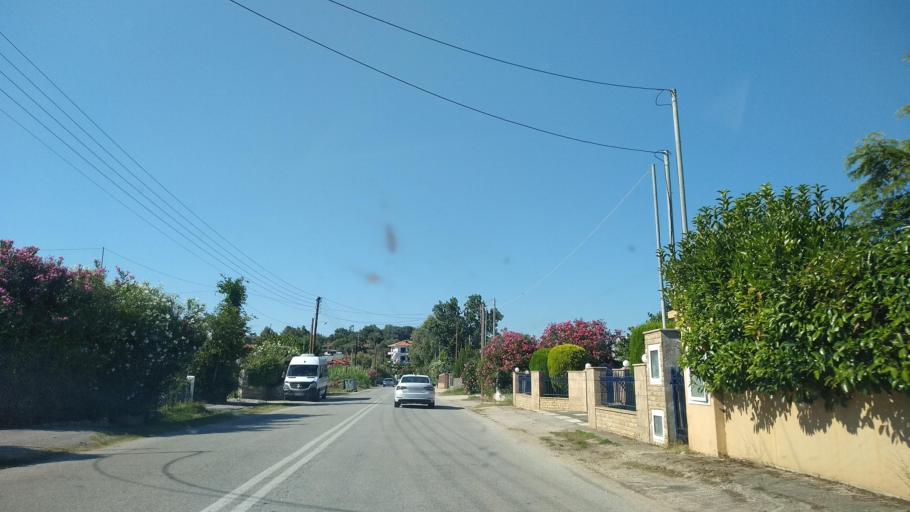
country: GR
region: Central Macedonia
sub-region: Nomos Chalkidikis
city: Agios Nikolaos
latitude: 40.2961
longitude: 23.6942
